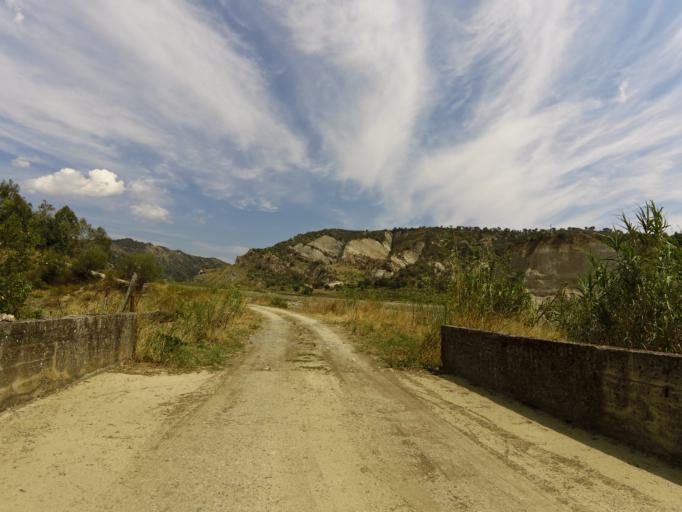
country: IT
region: Calabria
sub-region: Provincia di Reggio Calabria
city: Stilo
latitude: 38.4705
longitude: 16.4850
